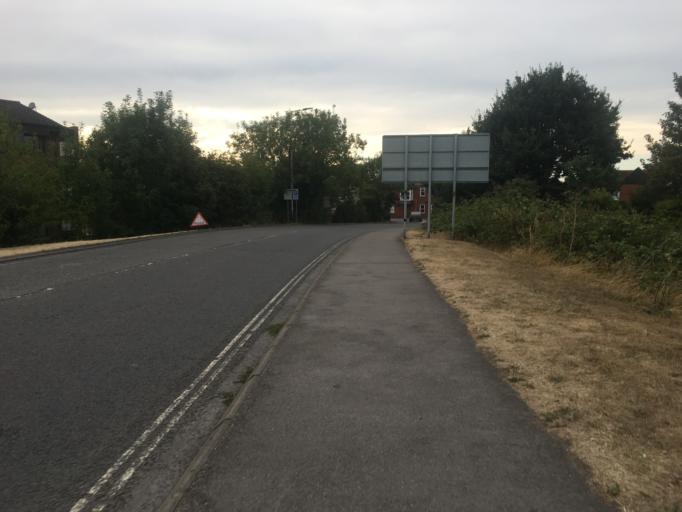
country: GB
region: England
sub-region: West Berkshire
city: Theale
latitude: 51.4375
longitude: -1.0719
